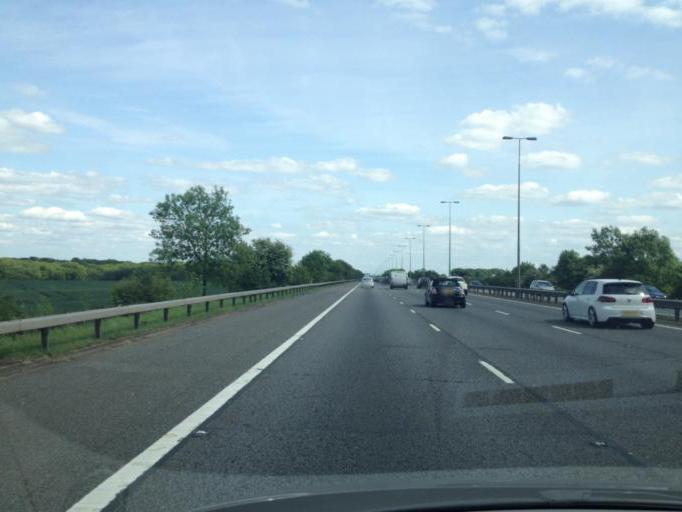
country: GB
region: England
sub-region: Buckinghamshire
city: Marlow
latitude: 51.6196
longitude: -0.8131
